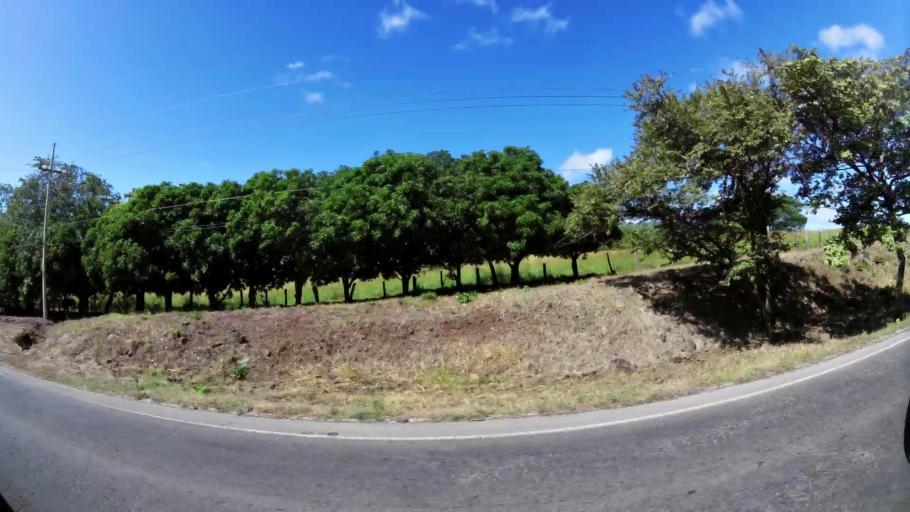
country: CR
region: Guanacaste
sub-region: Canton de Canas
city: Canas
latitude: 10.3926
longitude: -85.0805
